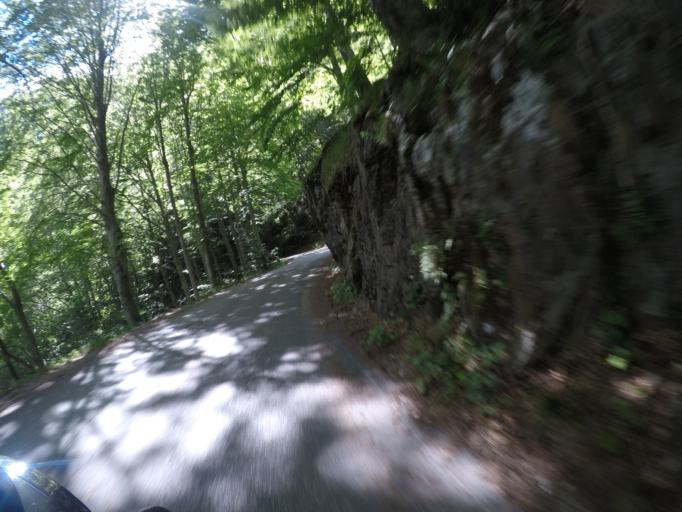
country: IT
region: Tuscany
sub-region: Provincia di Lucca
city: Minucciano
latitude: 44.1459
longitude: 10.1940
